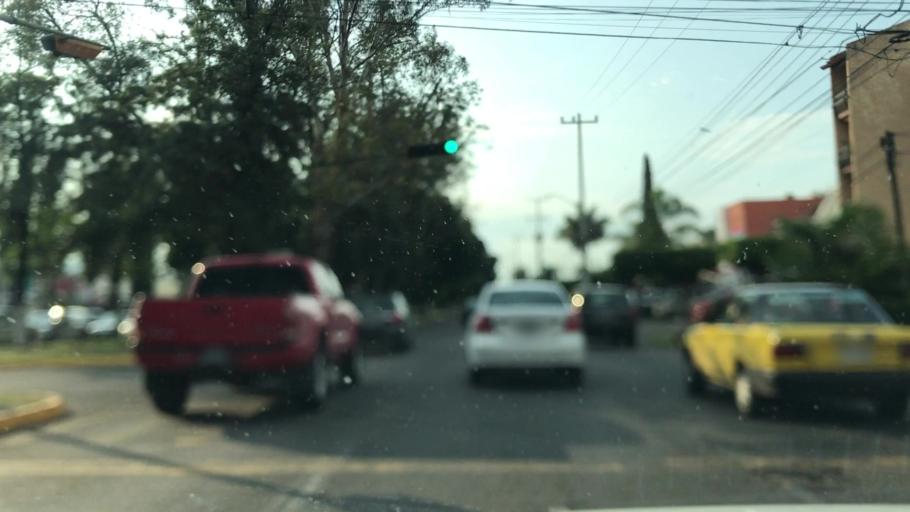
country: MX
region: Jalisco
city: Guadalajara
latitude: 20.6317
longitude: -103.4244
